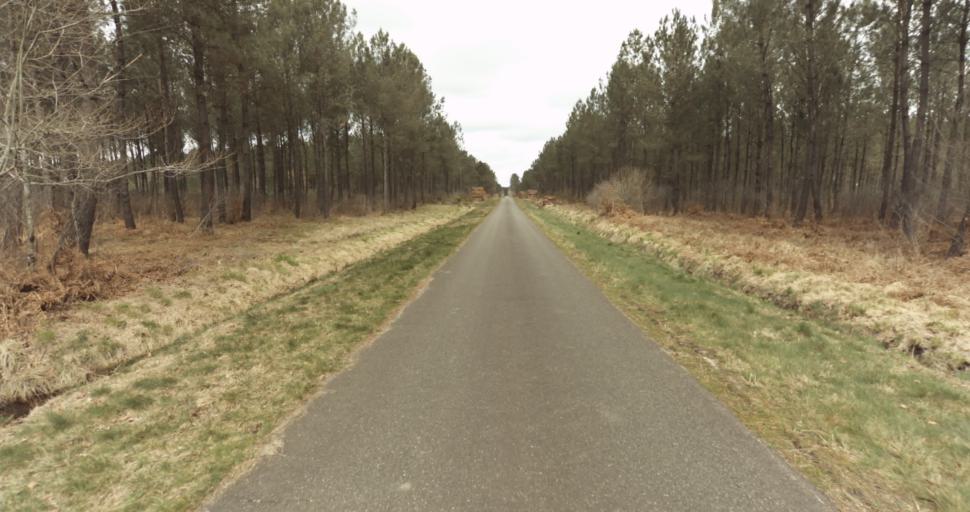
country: FR
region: Aquitaine
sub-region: Departement des Landes
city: Roquefort
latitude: 44.1014
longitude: -0.4541
